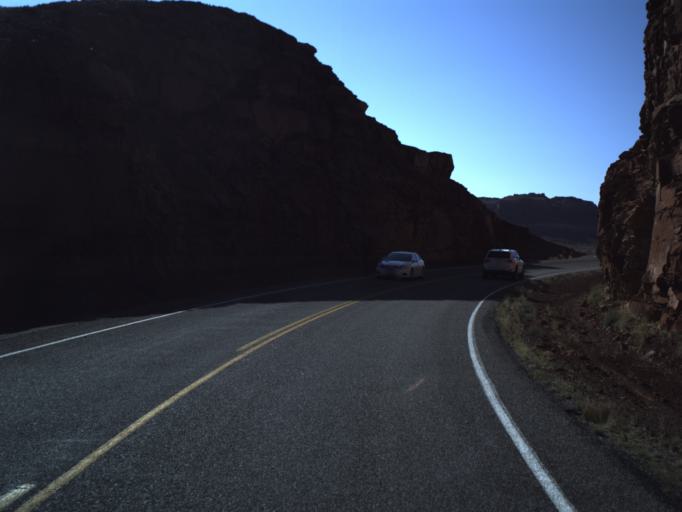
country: US
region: Utah
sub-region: San Juan County
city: Blanding
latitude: 37.8934
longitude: -110.3972
